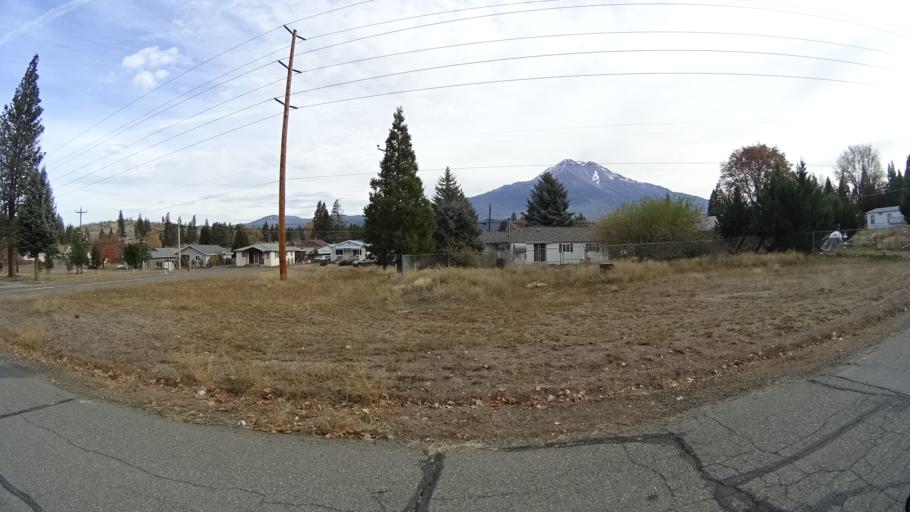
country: US
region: California
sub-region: Siskiyou County
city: Weed
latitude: 41.4377
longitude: -122.3893
